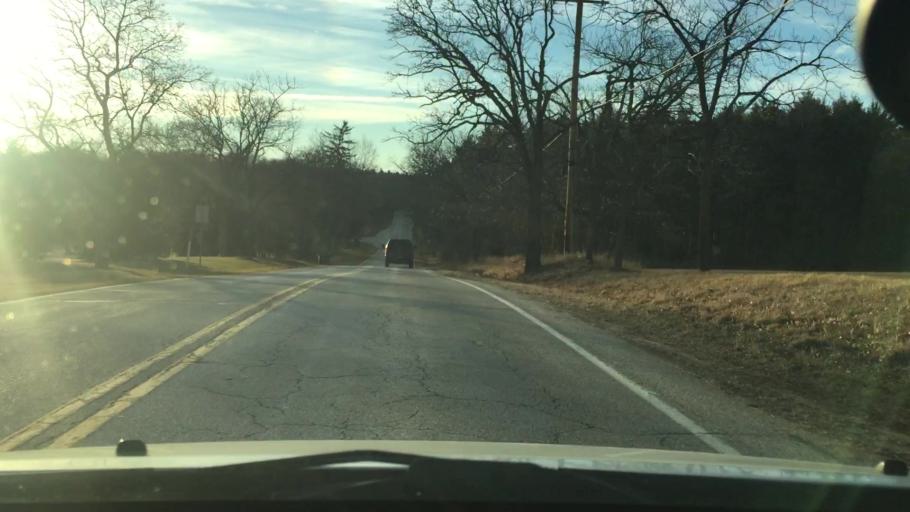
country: US
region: Wisconsin
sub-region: Waukesha County
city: North Prairie
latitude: 42.9427
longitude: -88.4281
